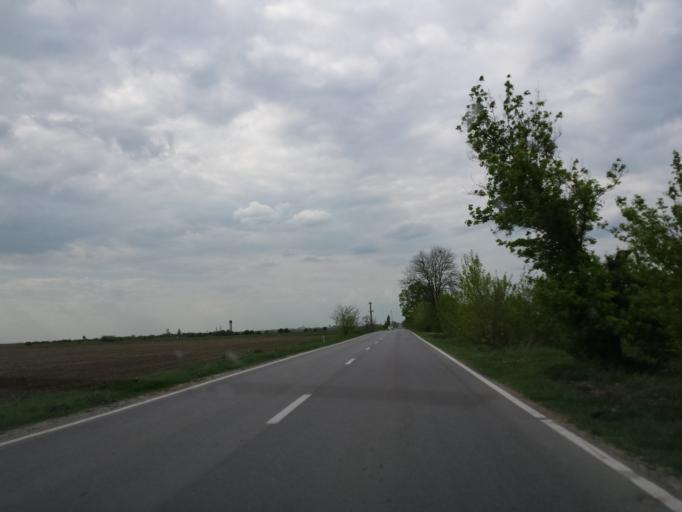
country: RO
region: Timis
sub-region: Comuna Sanpetru Mare
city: Sanpetru Mare
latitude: 46.0307
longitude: 20.6605
